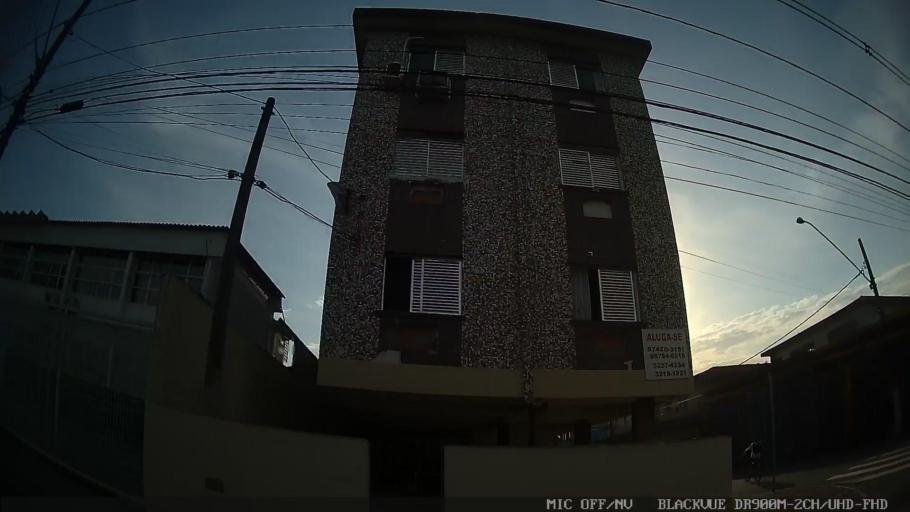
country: BR
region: Sao Paulo
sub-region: Cubatao
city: Cubatao
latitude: -23.9020
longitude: -46.4230
